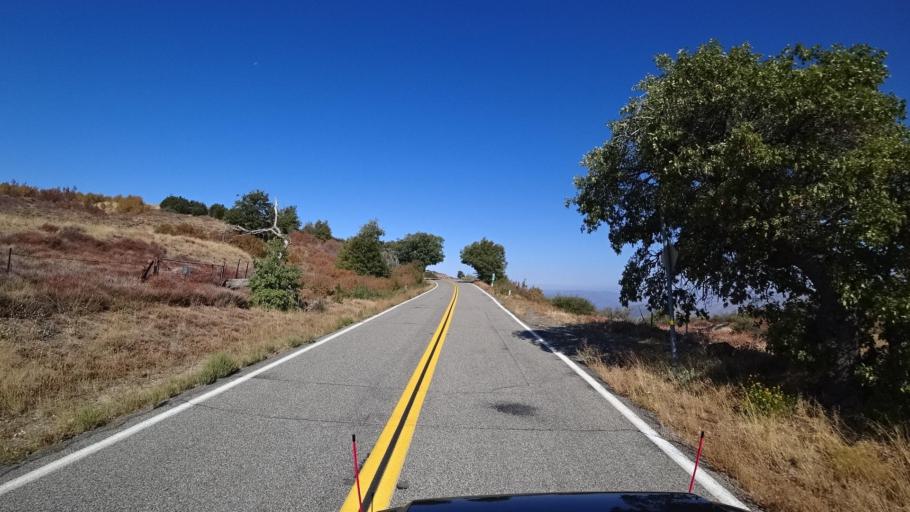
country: US
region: California
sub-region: San Diego County
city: Pine Valley
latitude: 32.9441
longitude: -116.4931
